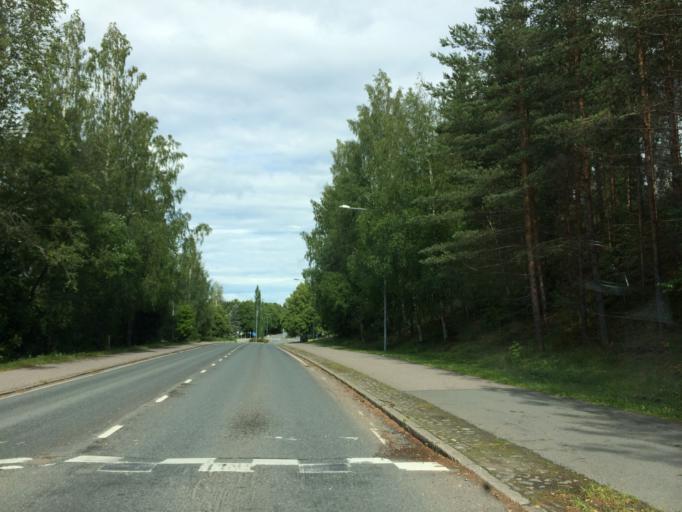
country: FI
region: Haeme
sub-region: Haemeenlinna
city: Turenki
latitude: 60.9193
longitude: 24.6422
